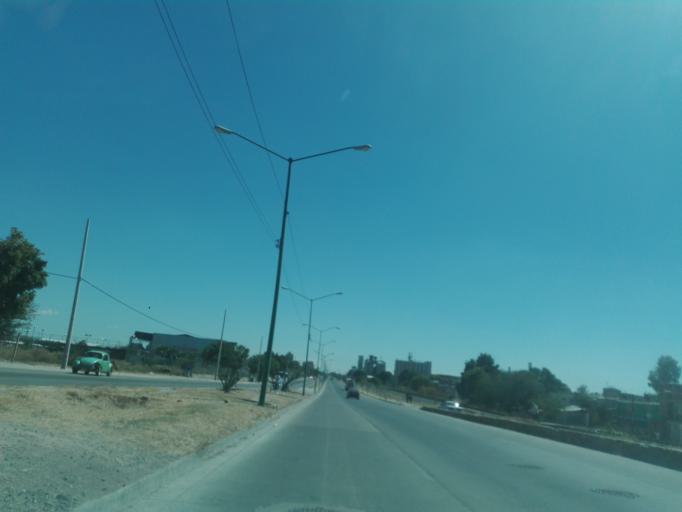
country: MX
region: Guanajuato
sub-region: Leon
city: San Jose de Duran (Los Troncoso)
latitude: 21.0890
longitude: -101.6743
